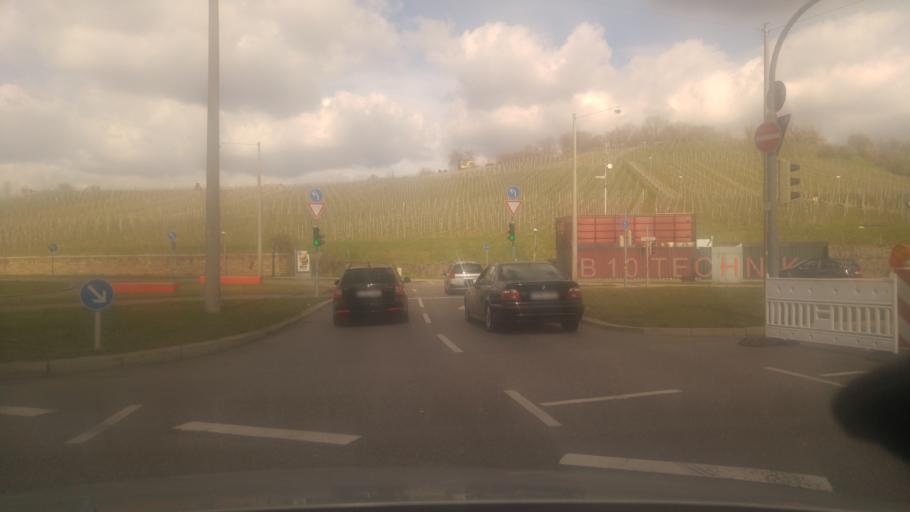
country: DE
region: Baden-Wuerttemberg
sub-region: Regierungsbezirk Stuttgart
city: Stuttgart Feuerbach
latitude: 48.8105
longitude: 9.1821
